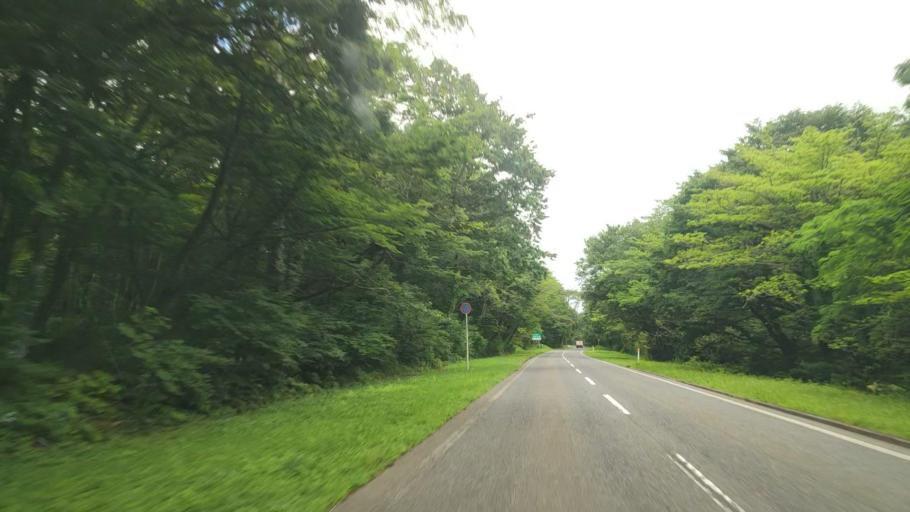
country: JP
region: Tottori
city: Yonago
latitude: 35.3987
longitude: 133.5063
